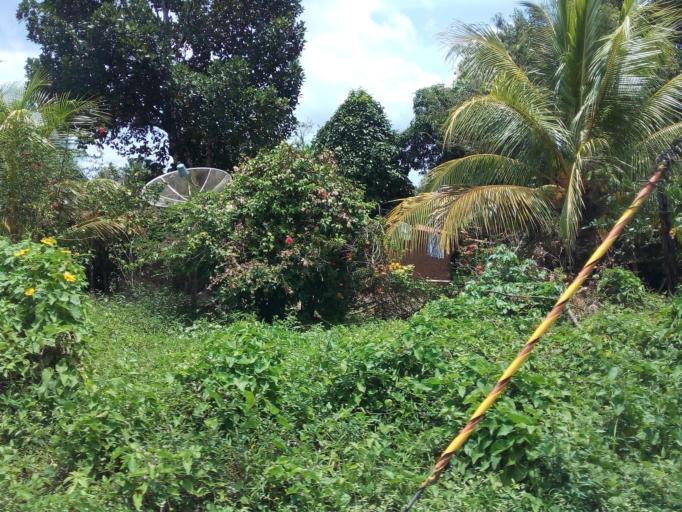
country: BR
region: Maranhao
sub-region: Anajatuba
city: Anajatuba
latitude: -3.0358
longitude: -44.3470
